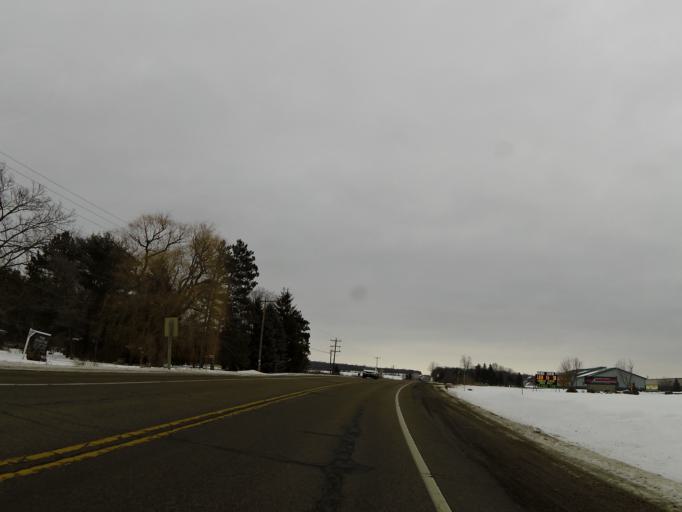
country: US
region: Minnesota
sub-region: Washington County
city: Stillwater
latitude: 45.0716
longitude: -92.7882
